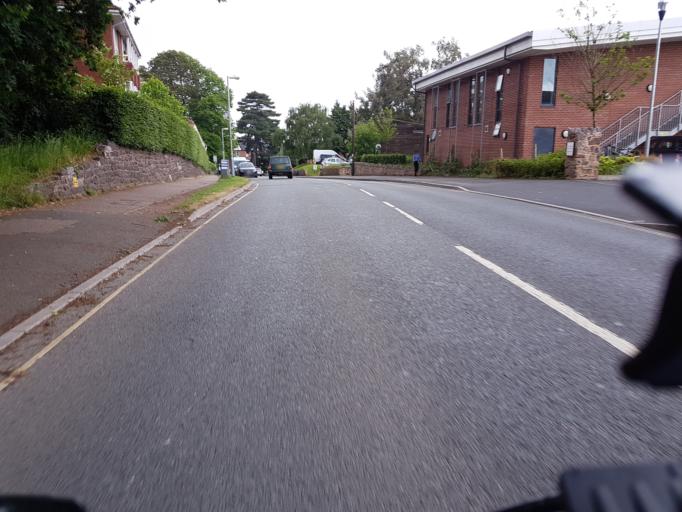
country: GB
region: England
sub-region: Devon
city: Exeter
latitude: 50.7340
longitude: -3.5292
